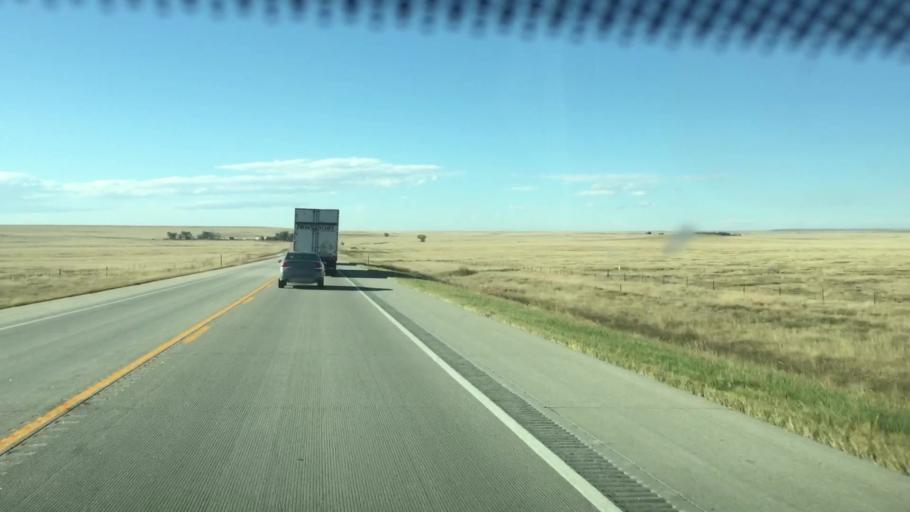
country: US
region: Colorado
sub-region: Lincoln County
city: Hugo
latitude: 38.9263
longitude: -103.1923
